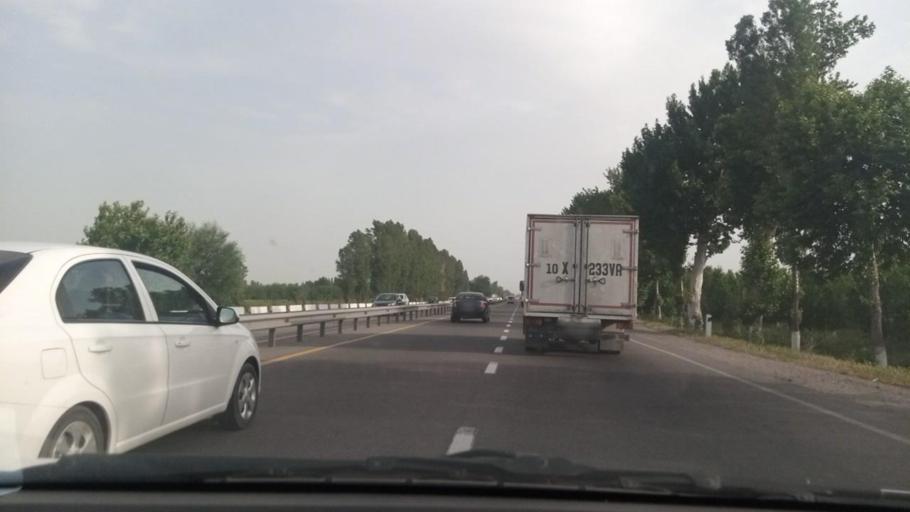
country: UZ
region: Toshkent Shahri
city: Bektemir
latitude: 41.2151
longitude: 69.4026
